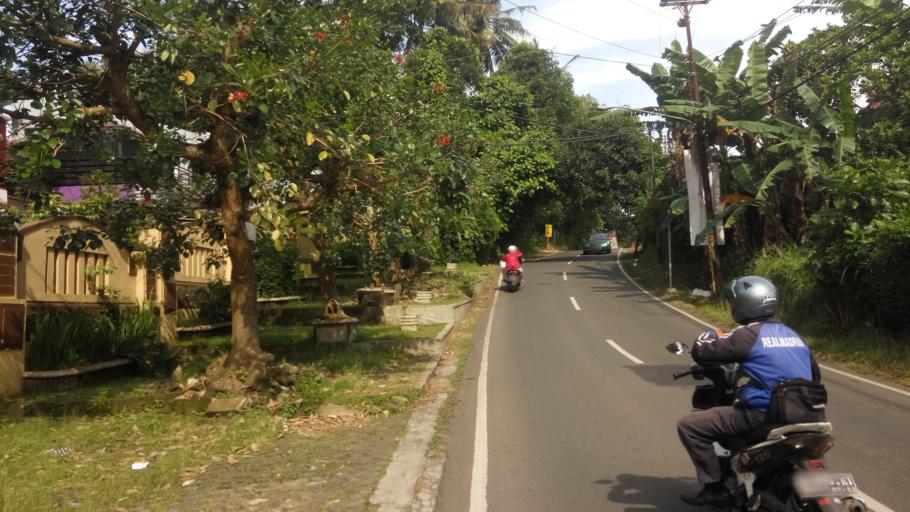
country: ID
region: Central Java
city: Ungaran
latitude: -7.1425
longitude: 110.4136
